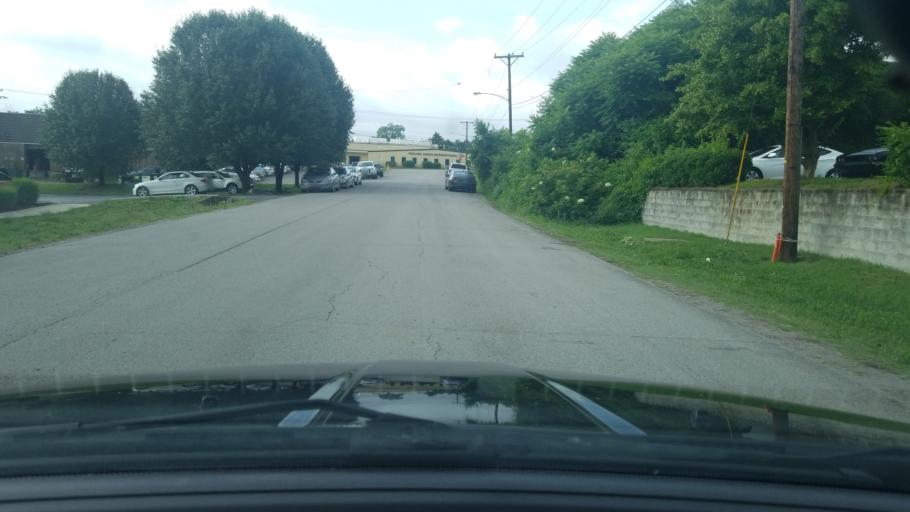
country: US
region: Tennessee
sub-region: Davidson County
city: Oak Hill
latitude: 36.0939
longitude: -86.7429
